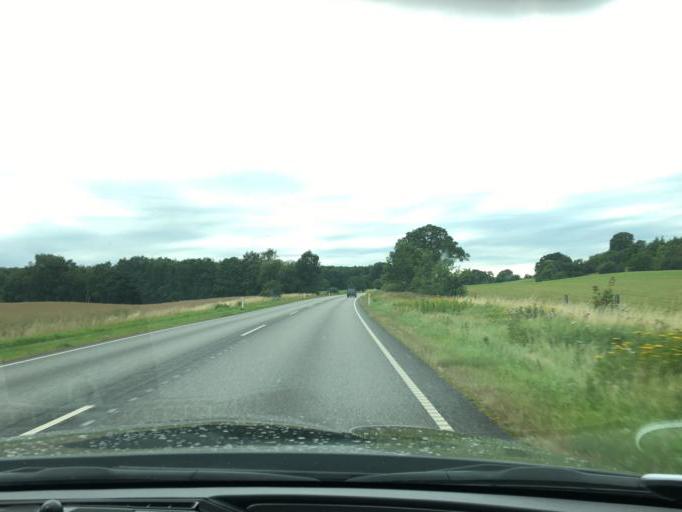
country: DK
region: Capital Region
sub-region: Horsholm Kommune
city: Horsholm
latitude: 55.8779
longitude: 12.4705
